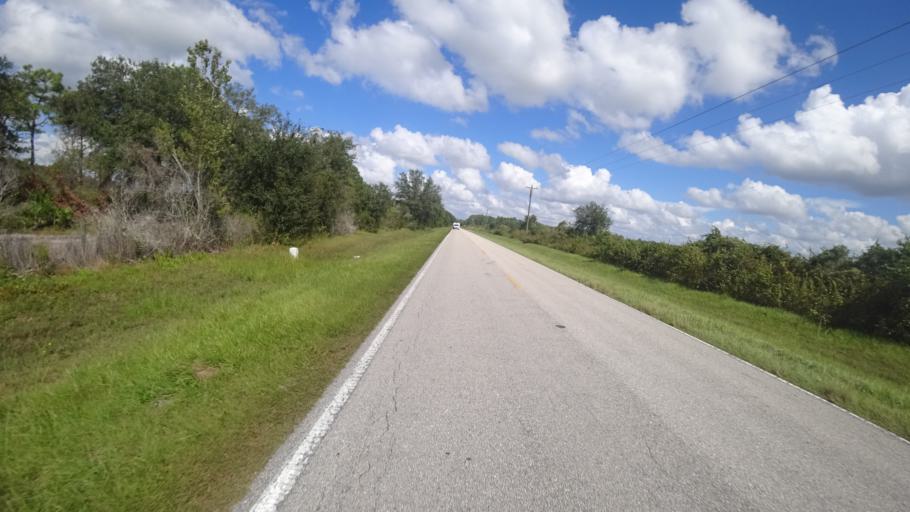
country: US
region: Florida
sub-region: Sarasota County
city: Lake Sarasota
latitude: 27.3770
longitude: -82.1402
